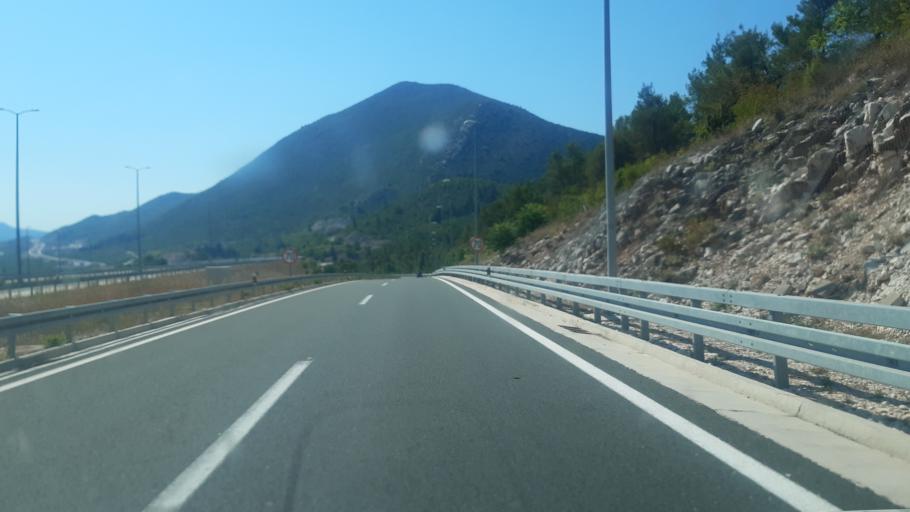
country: BA
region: Federation of Bosnia and Herzegovina
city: Ljubuski
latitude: 43.1509
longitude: 17.4823
